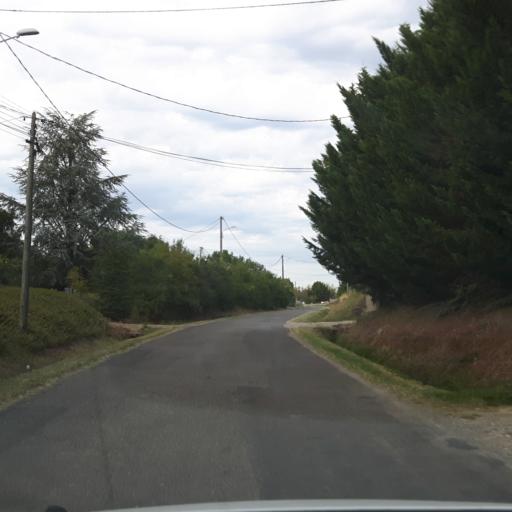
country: FR
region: Midi-Pyrenees
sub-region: Departement de la Haute-Garonne
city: Fronton
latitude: 43.8314
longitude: 1.3779
